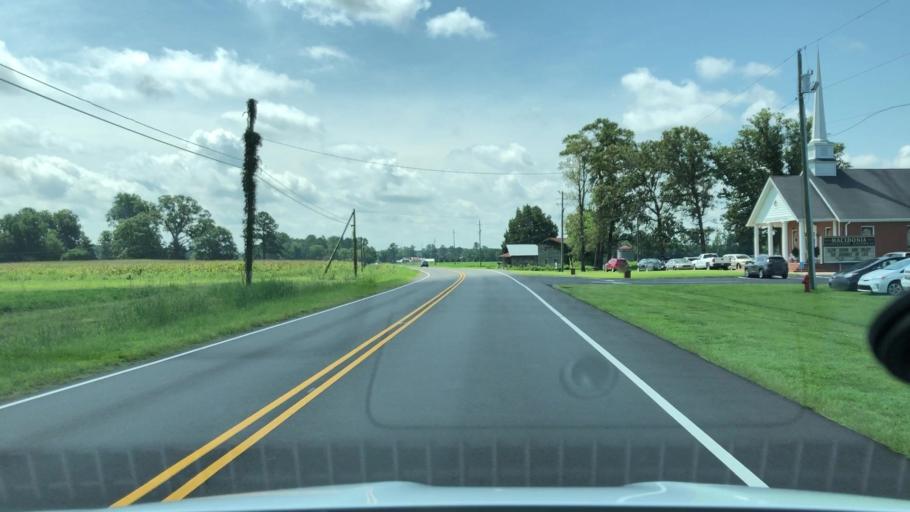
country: US
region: North Carolina
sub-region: Martin County
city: Williamston
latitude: 35.7504
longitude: -77.0758
